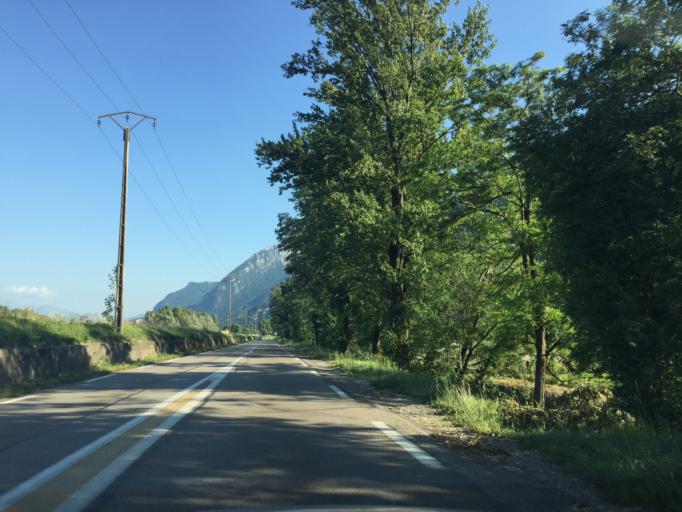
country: FR
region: Rhone-Alpes
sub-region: Departement de l'Isere
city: Veurey-Voroize
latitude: 45.2771
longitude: 5.6181
